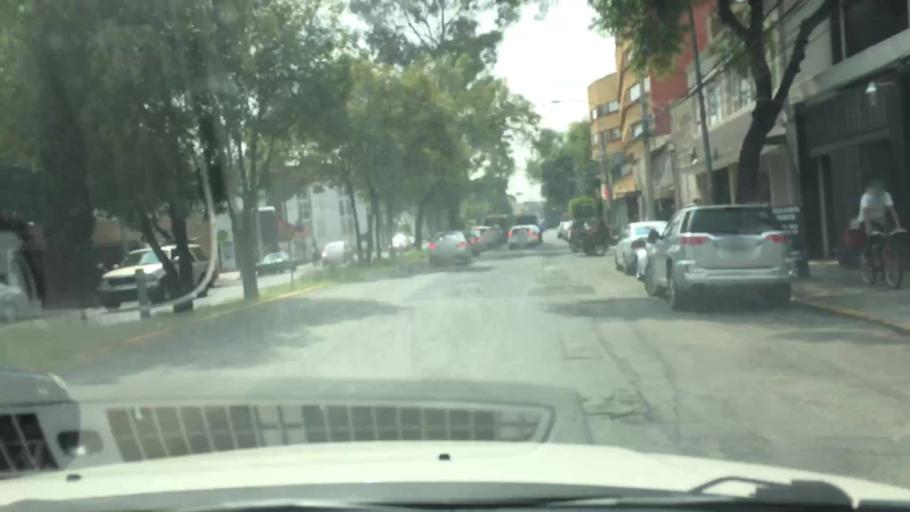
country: MX
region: Mexico City
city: Coyoacan
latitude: 19.3381
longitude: -99.1507
